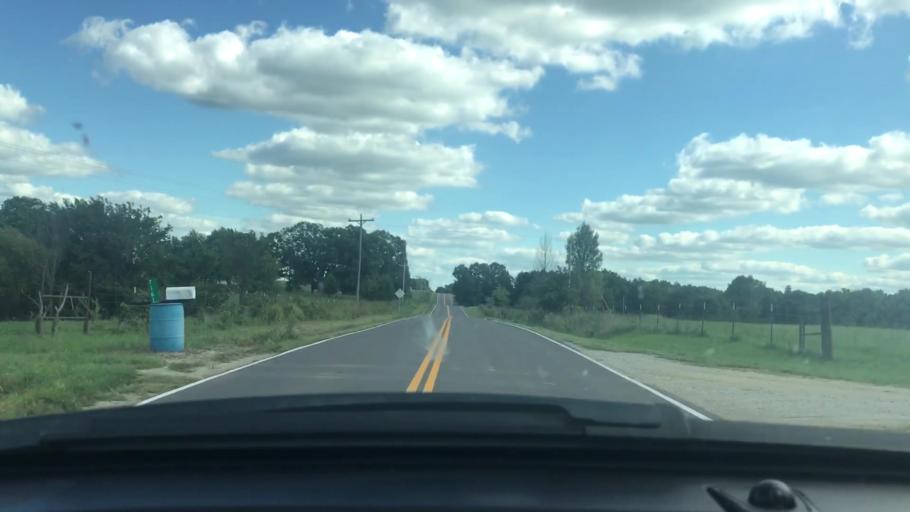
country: US
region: Missouri
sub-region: Wright County
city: Mountain Grove
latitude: 37.3125
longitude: -92.3181
